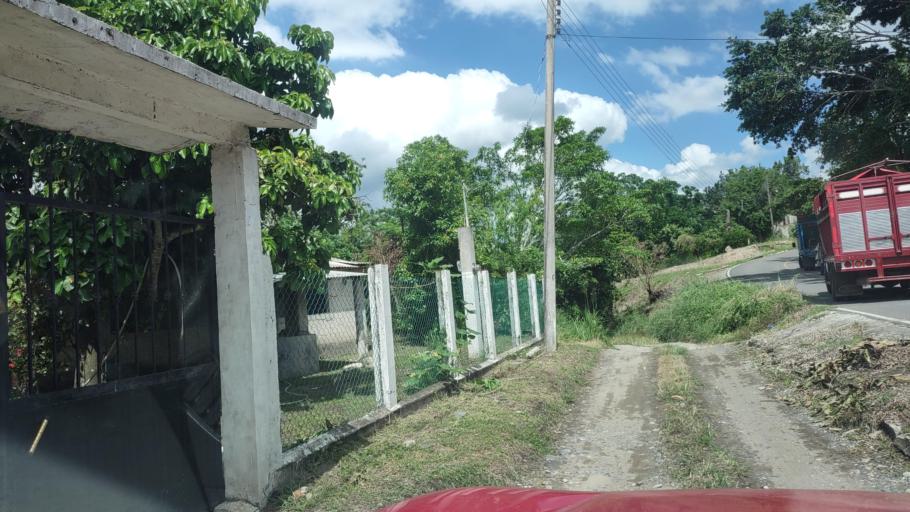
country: MX
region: Puebla
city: San Jose Acateno
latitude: 20.2171
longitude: -97.1357
